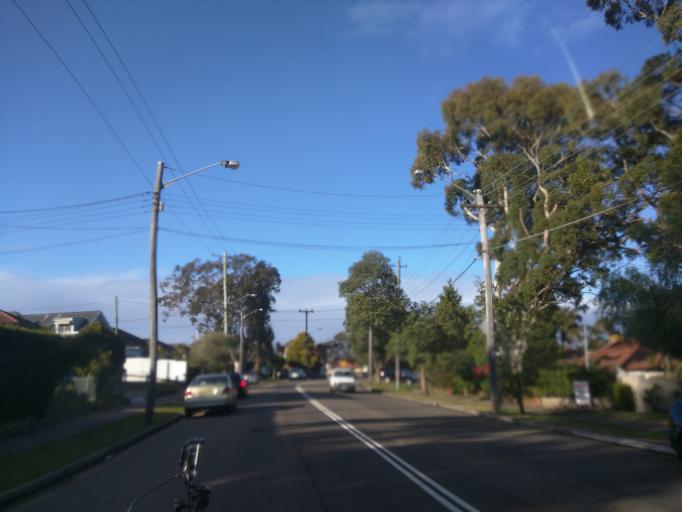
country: AU
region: New South Wales
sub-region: Hurstville
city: Peakhurst
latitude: -33.9655
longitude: 151.0497
